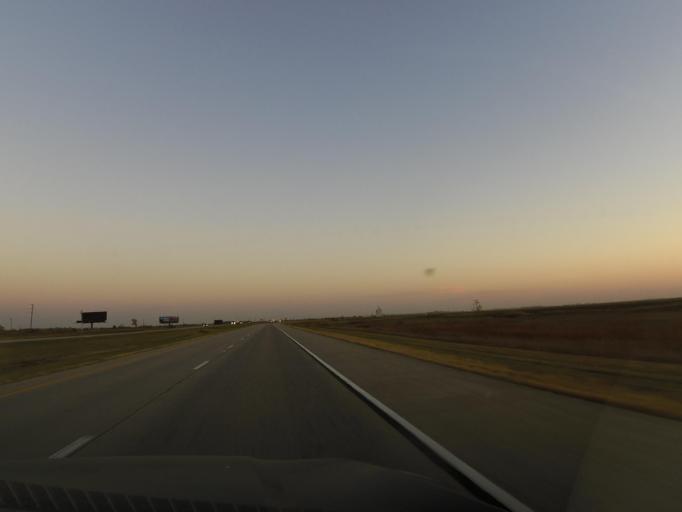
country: US
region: North Dakota
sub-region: Traill County
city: Hillsboro
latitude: 47.3821
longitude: -97.0600
